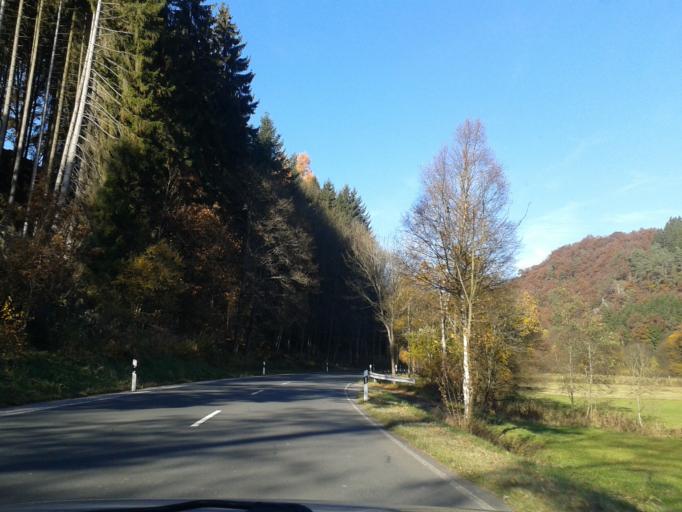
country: DE
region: North Rhine-Westphalia
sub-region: Regierungsbezirk Arnsberg
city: Bad Laasphe
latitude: 50.8782
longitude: 8.3478
